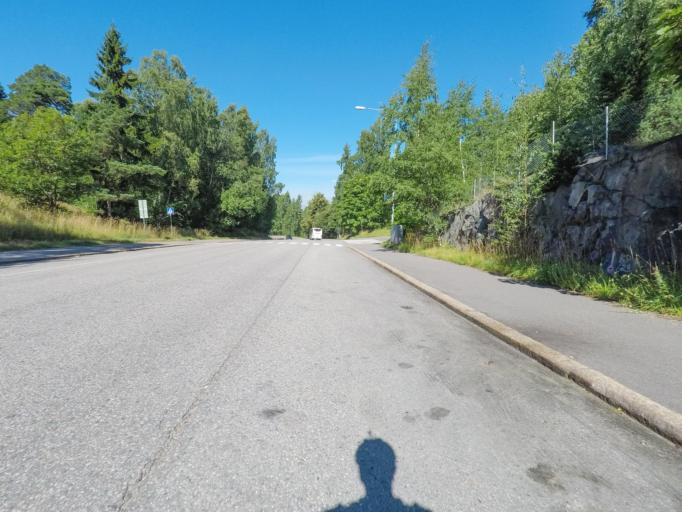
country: FI
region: Uusimaa
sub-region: Helsinki
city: Helsinki
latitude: 60.1762
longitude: 25.0373
